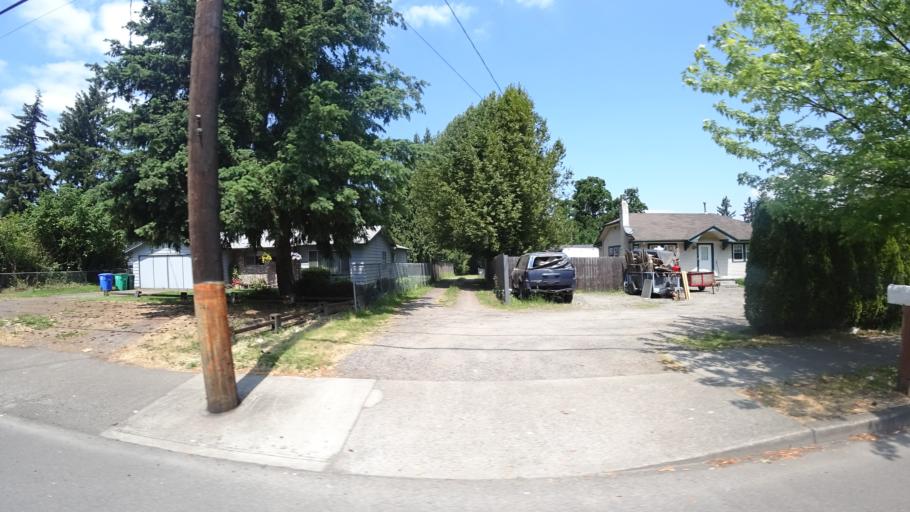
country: US
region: Oregon
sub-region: Multnomah County
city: Fairview
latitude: 45.5337
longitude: -122.4994
